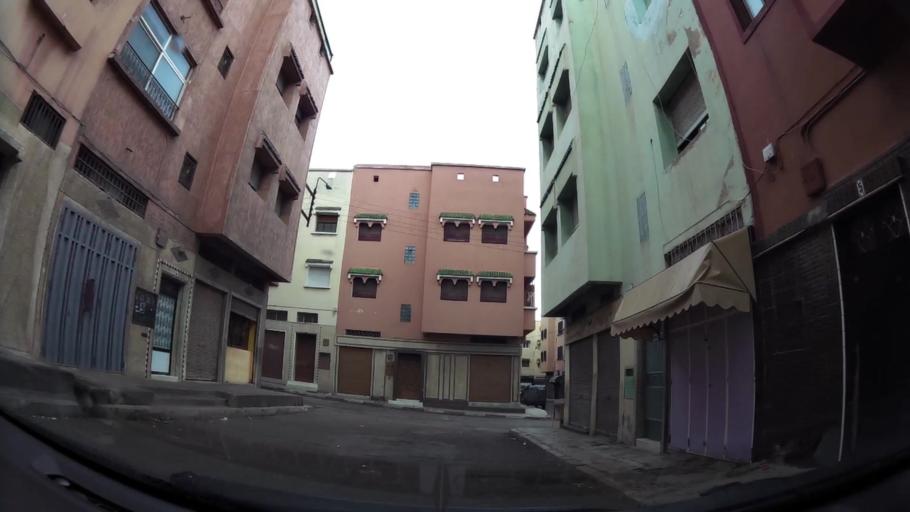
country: MA
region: Grand Casablanca
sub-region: Casablanca
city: Casablanca
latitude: 33.5454
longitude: -7.5857
